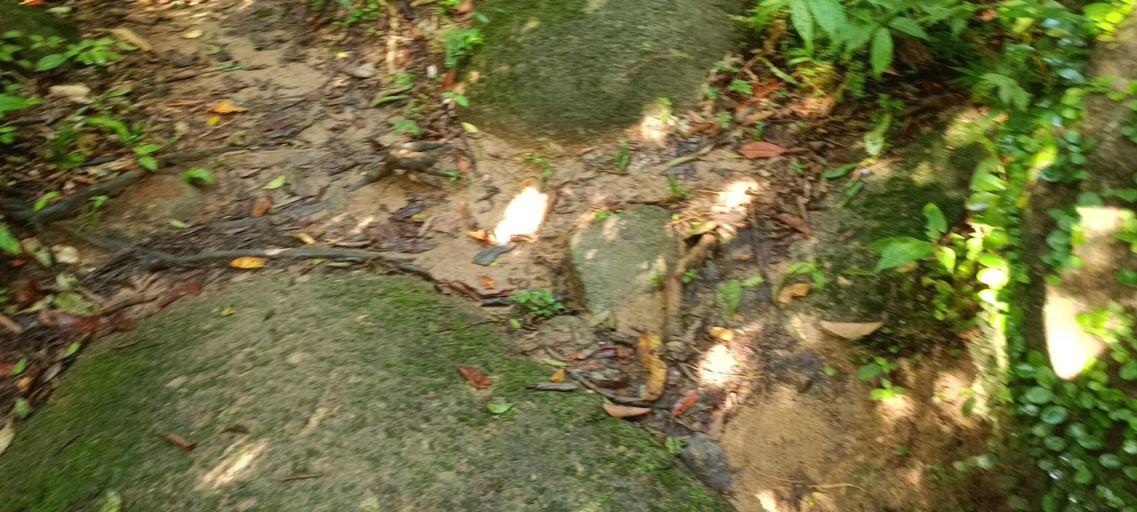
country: MY
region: Penang
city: Bukit Mertajam
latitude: 5.3645
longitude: 100.4874
